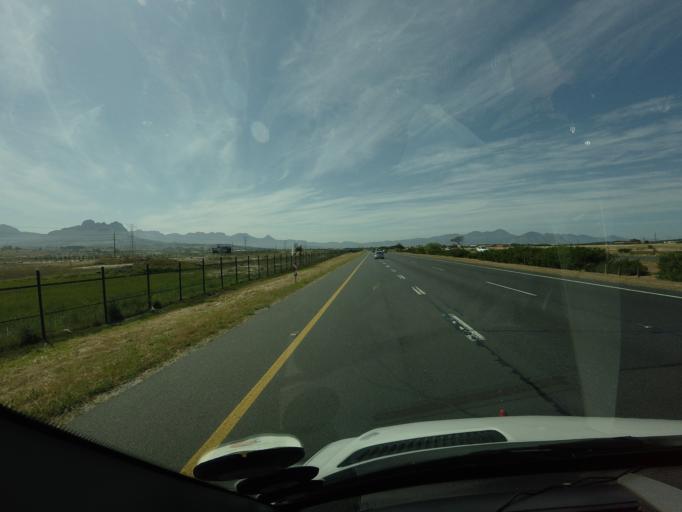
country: ZA
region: Western Cape
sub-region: Cape Winelands District Municipality
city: Stellenbosch
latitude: -34.0521
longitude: 18.7633
